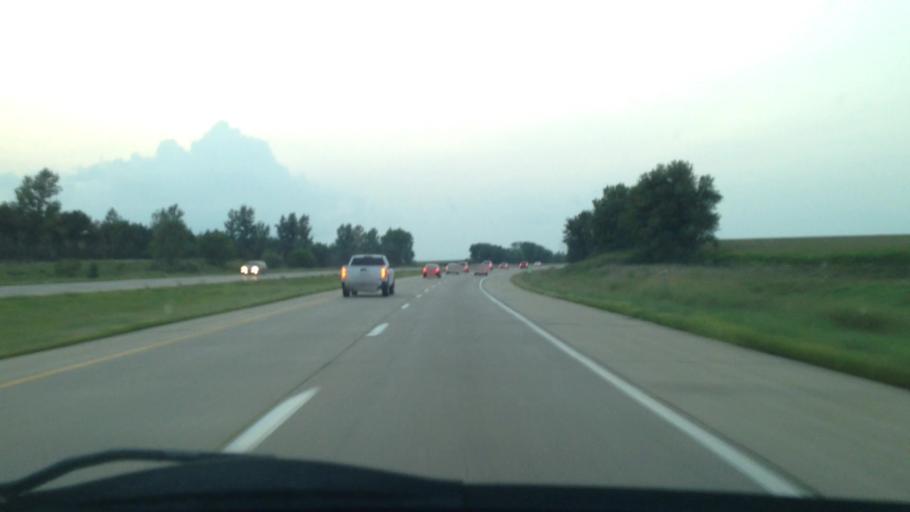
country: US
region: Iowa
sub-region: Black Hawk County
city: Elk Run Heights
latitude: 42.4205
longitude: -92.1817
